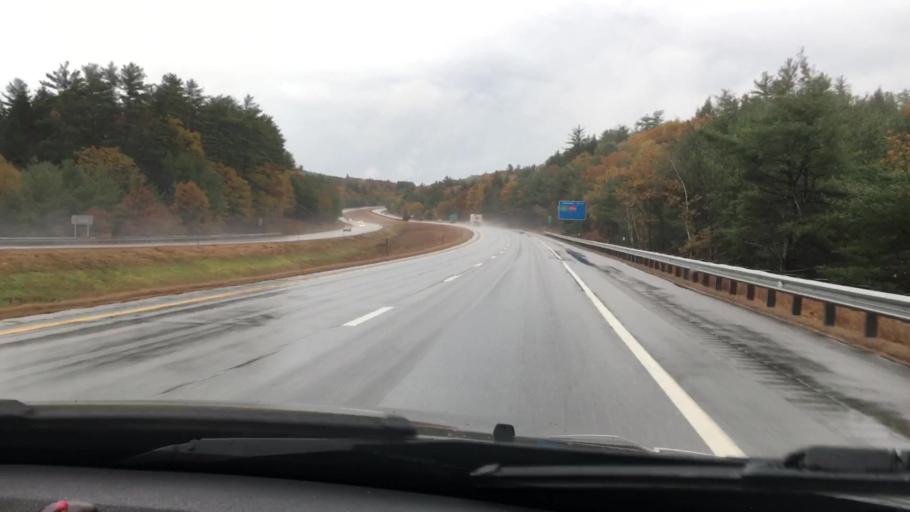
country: US
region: New Hampshire
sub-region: Grafton County
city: Ashland
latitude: 43.6275
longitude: -71.6515
